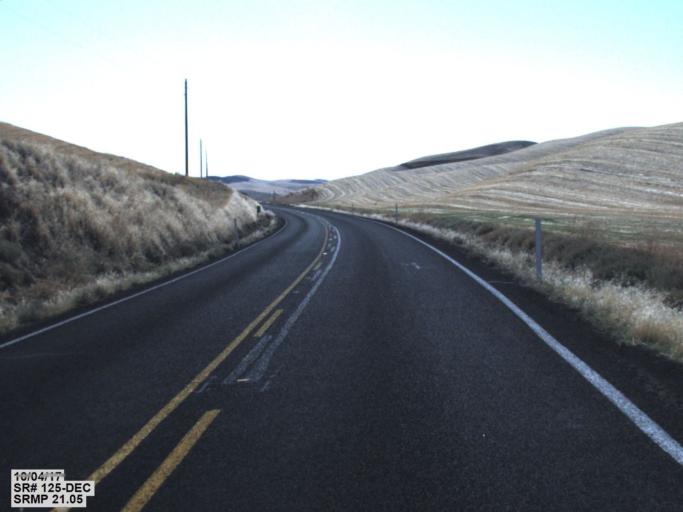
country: US
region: Washington
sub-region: Walla Walla County
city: Walla Walla
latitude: 46.2628
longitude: -118.3533
